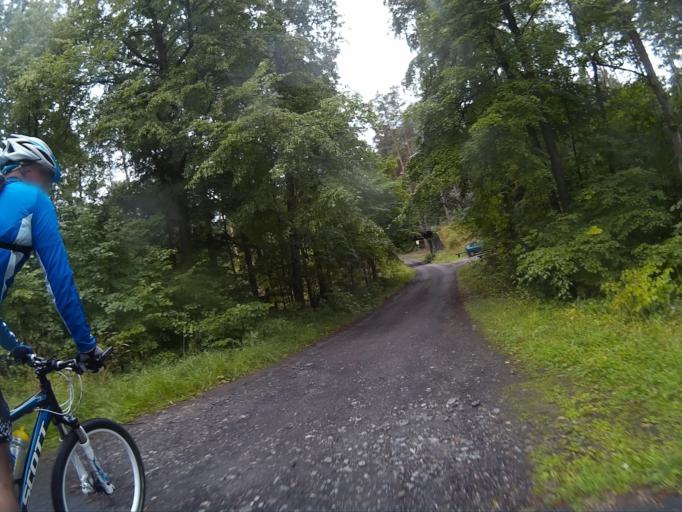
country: PL
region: Kujawsko-Pomorskie
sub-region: Powiat swiecki
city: Osie
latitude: 53.6092
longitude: 18.3040
